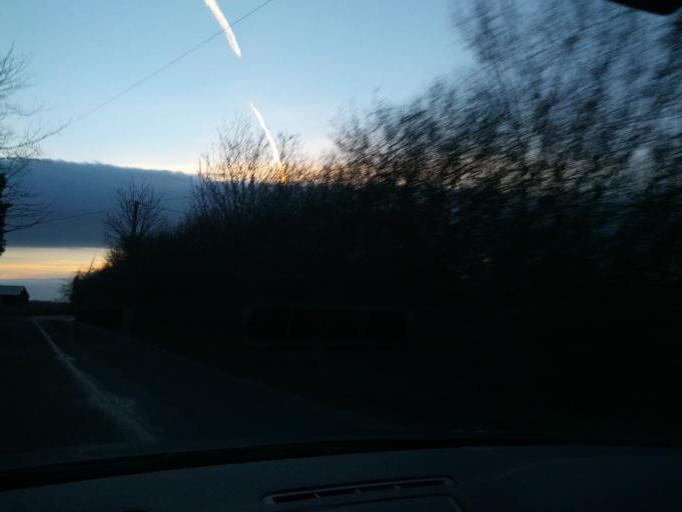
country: IE
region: Leinster
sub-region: Uibh Fhaili
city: Banagher
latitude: 53.1063
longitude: -8.0587
